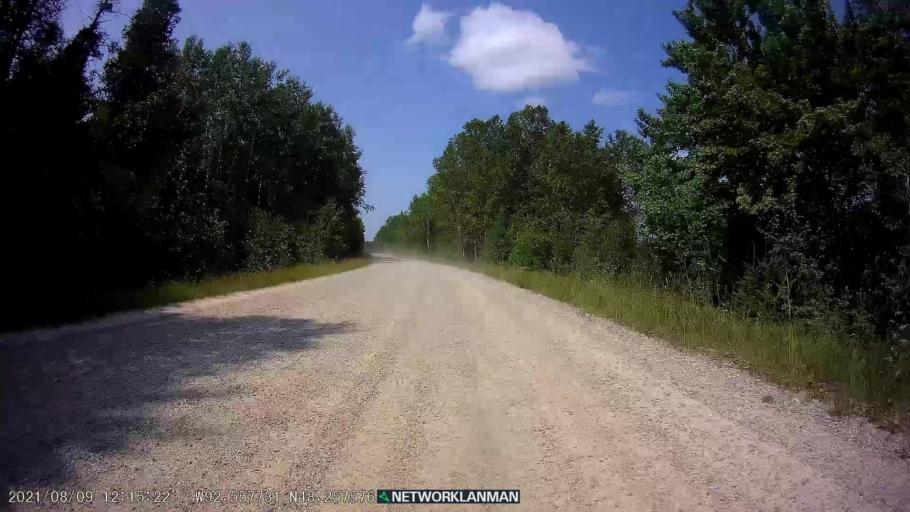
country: US
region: Minnesota
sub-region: Saint Louis County
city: Parkville
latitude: 48.2575
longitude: -92.5578
